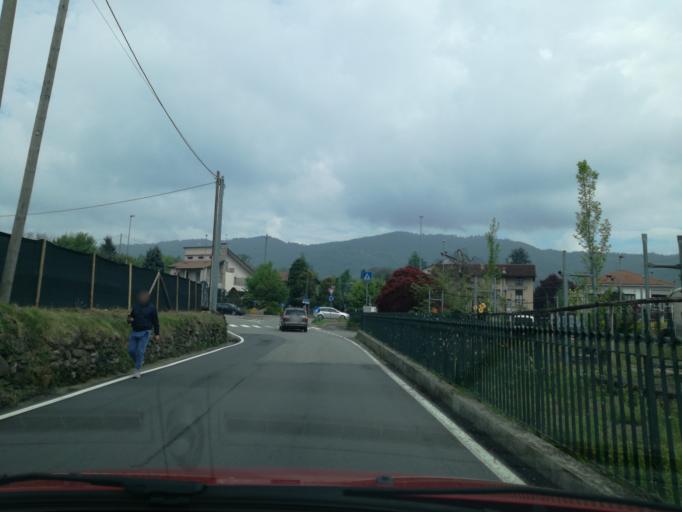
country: IT
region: Lombardy
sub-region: Provincia di Lecco
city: Olgiate Molgora
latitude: 45.7306
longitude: 9.3910
